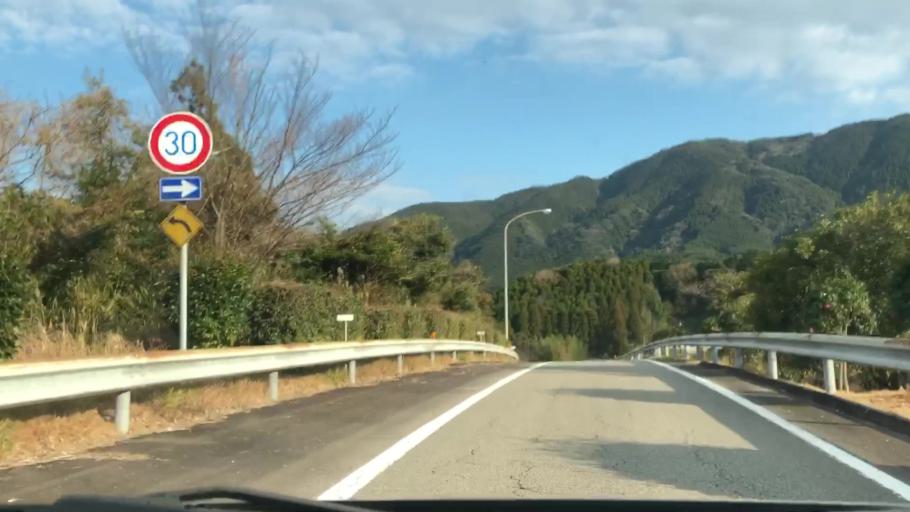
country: JP
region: Miyazaki
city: Miyazaki-shi
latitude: 31.8222
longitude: 131.3020
